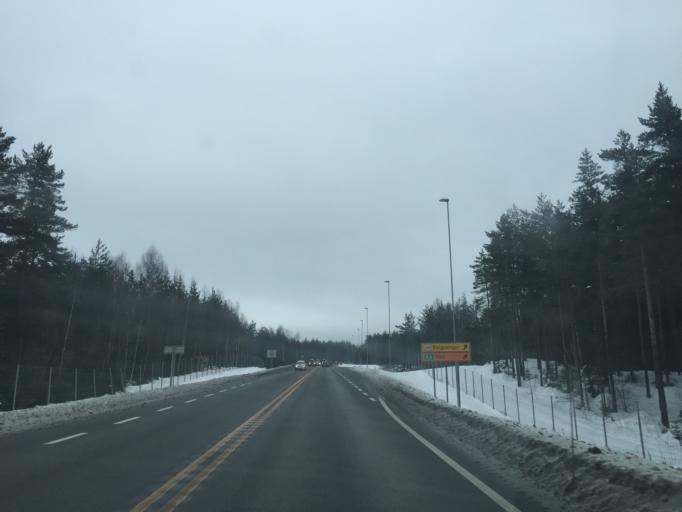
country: NO
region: Hedmark
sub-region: Stange
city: Stange
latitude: 60.7111
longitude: 11.2809
